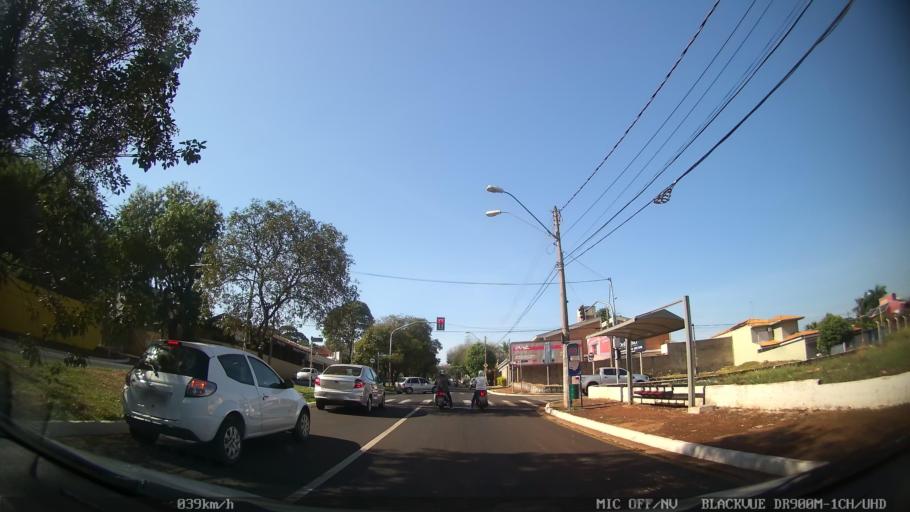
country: BR
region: Sao Paulo
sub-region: Ribeirao Preto
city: Ribeirao Preto
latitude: -21.1962
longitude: -47.8206
